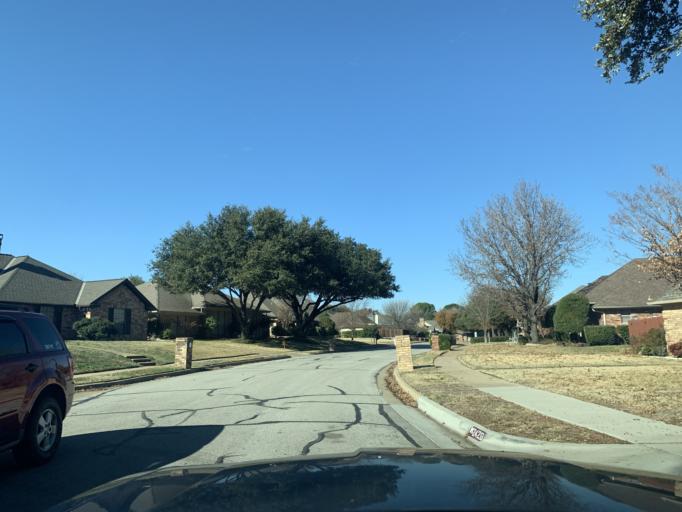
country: US
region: Texas
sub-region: Tarrant County
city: Bedford
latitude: 32.8477
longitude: -97.1545
